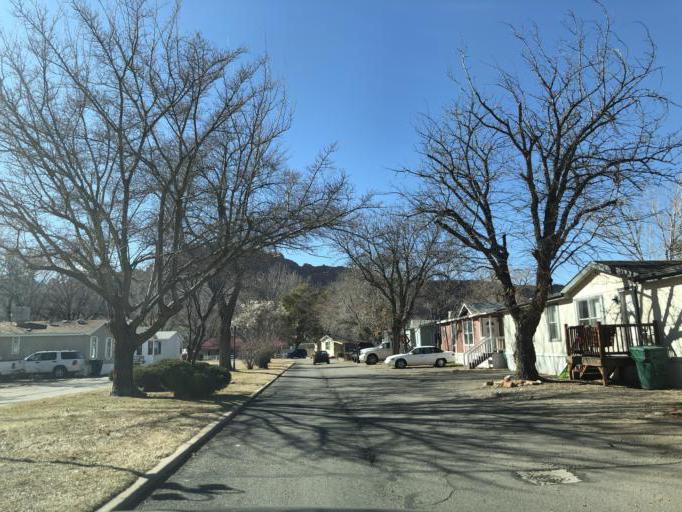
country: US
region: Utah
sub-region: Grand County
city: Moab
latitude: 38.5772
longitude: -109.5621
